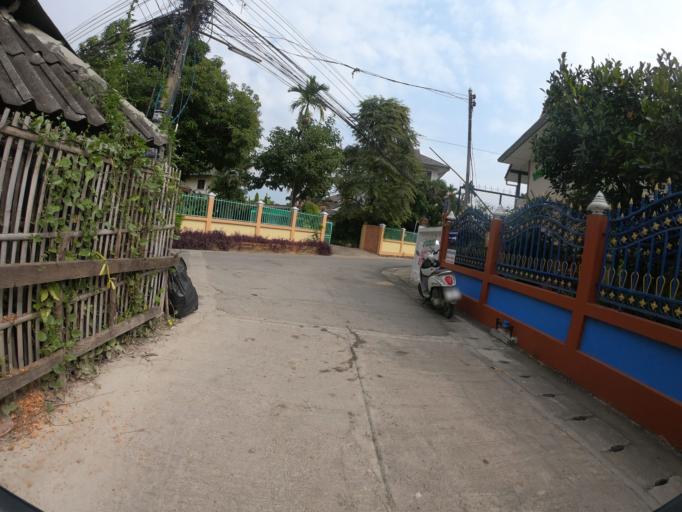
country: TH
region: Chiang Mai
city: Hang Dong
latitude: 18.7392
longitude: 98.9301
